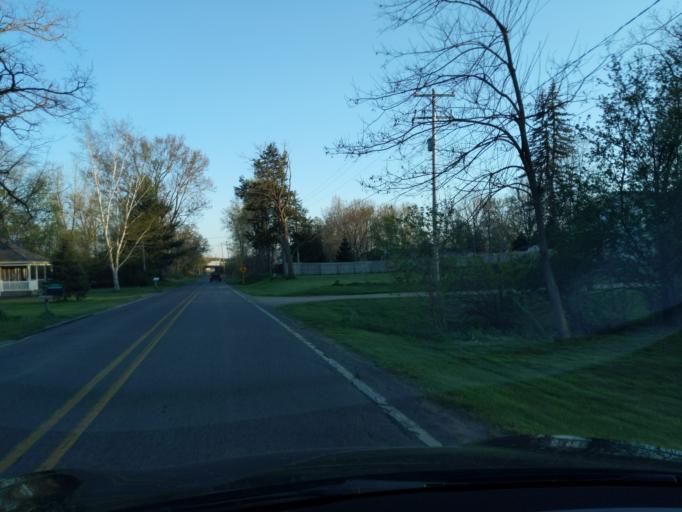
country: US
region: Michigan
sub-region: Jackson County
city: Jackson
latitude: 42.2577
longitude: -84.4833
